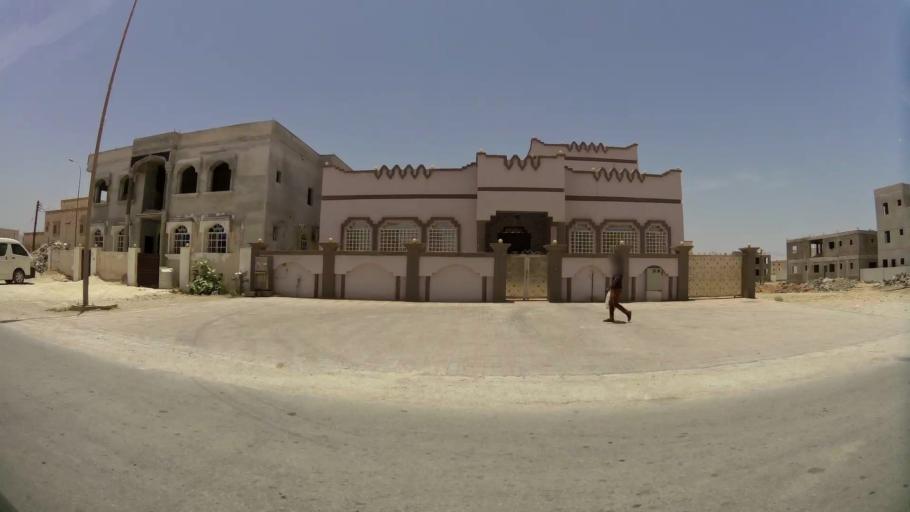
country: OM
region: Zufar
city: Salalah
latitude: 17.0923
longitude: 54.1561
